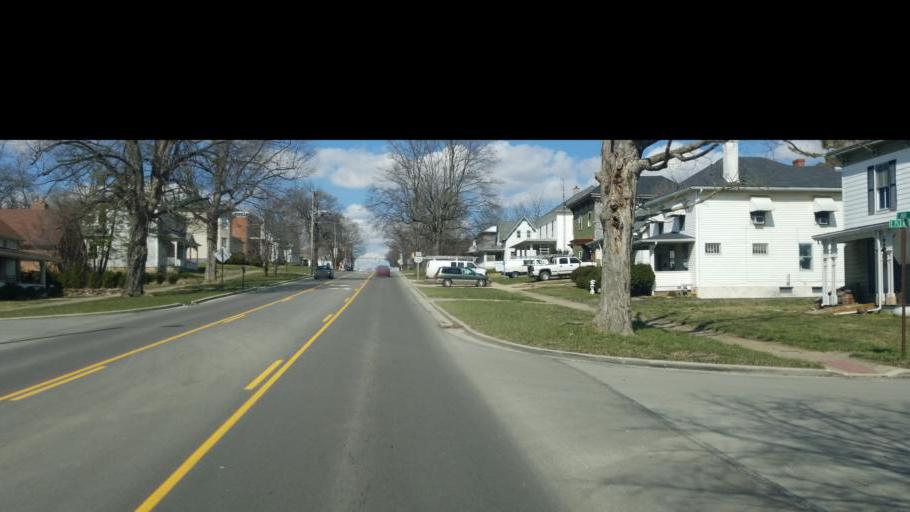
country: US
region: Ohio
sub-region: Highland County
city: Hillsboro
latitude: 39.1981
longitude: -83.6125
